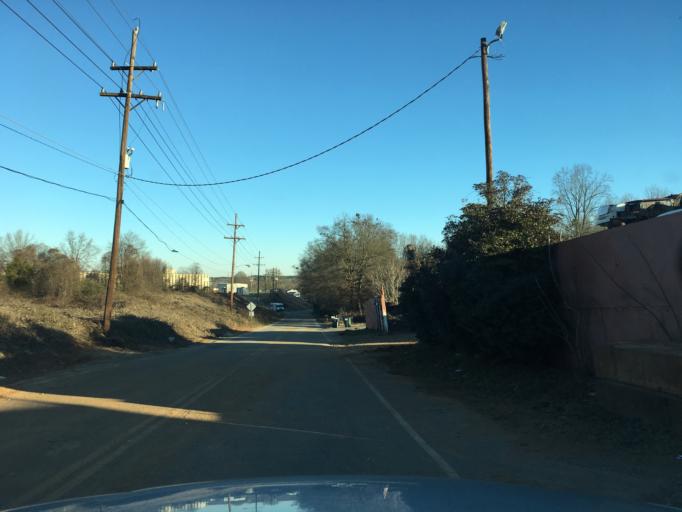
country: US
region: South Carolina
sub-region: Spartanburg County
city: Wellford
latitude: 34.9185
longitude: -82.1093
